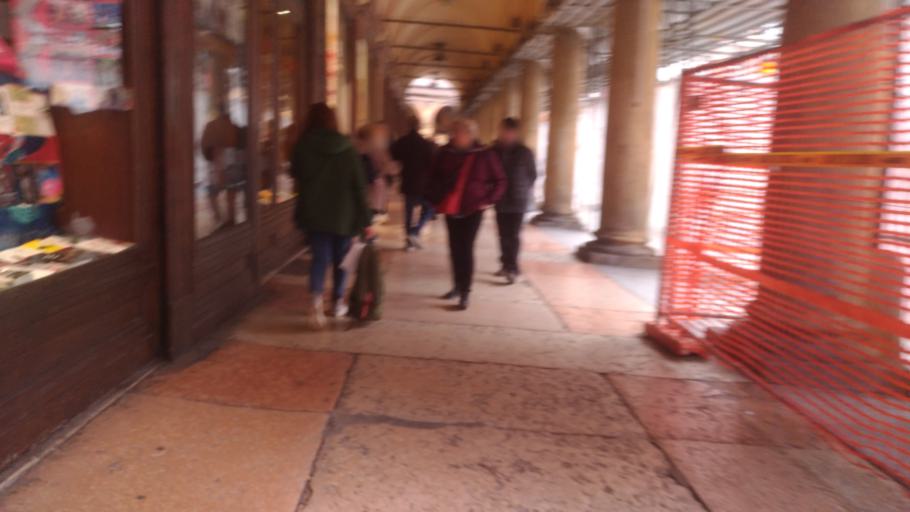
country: IT
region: Emilia-Romagna
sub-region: Provincia di Bologna
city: Bologna
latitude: 44.4920
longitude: 11.3432
